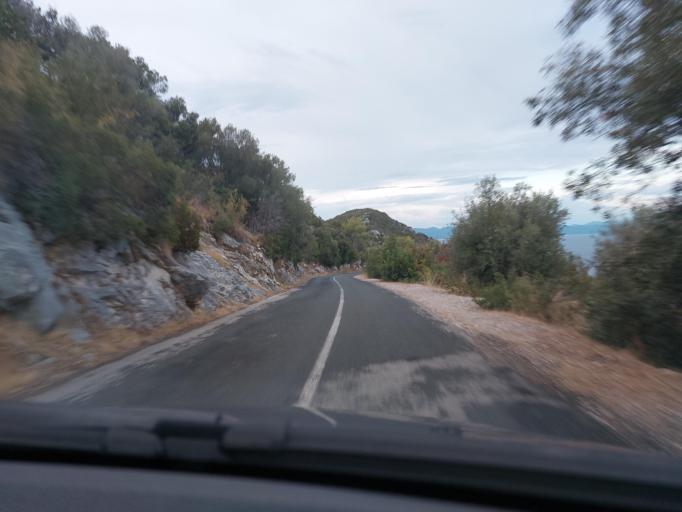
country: HR
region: Dubrovacko-Neretvanska
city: Smokvica
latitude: 42.7717
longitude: 16.8784
